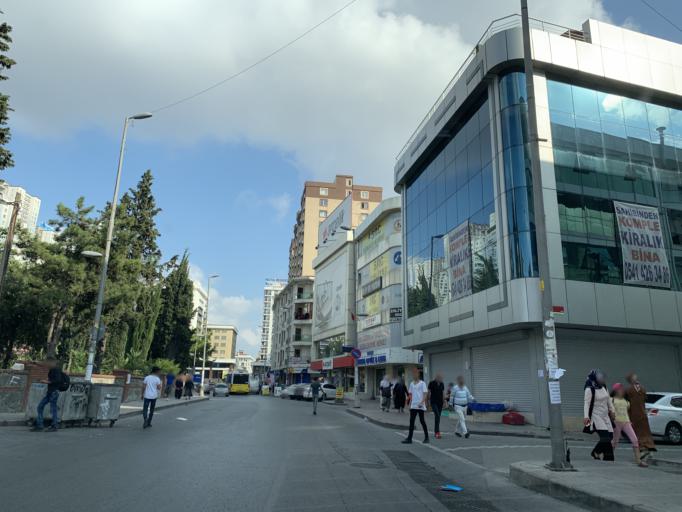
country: TR
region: Istanbul
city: Esenyurt
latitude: 41.0325
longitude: 28.6798
